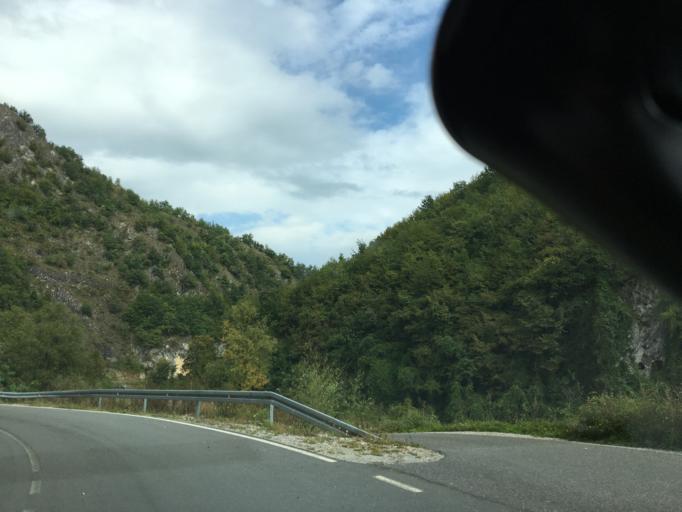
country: ME
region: Berane
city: Berane
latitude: 42.8291
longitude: 19.8346
